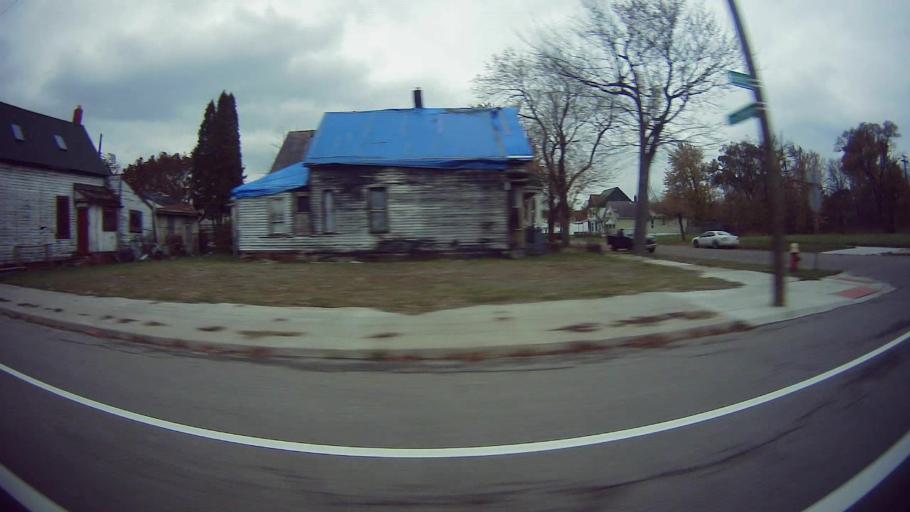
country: US
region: Michigan
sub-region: Wayne County
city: Hamtramck
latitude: 42.3648
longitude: -83.0362
